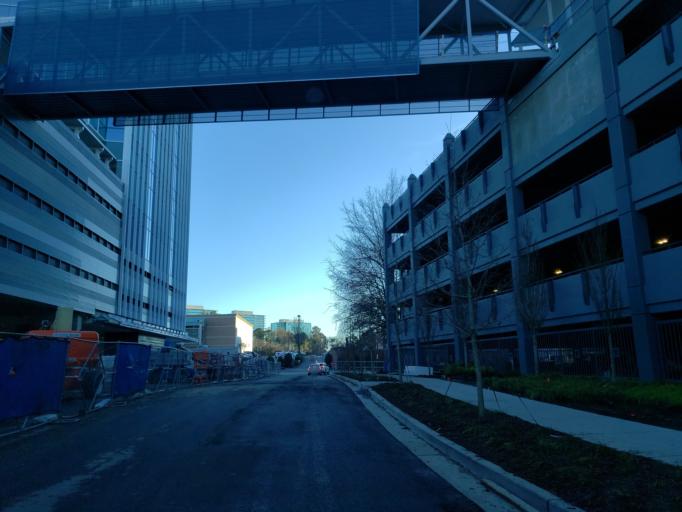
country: US
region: Georgia
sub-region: DeKalb County
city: Dunwoody
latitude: 33.9214
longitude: -84.3436
